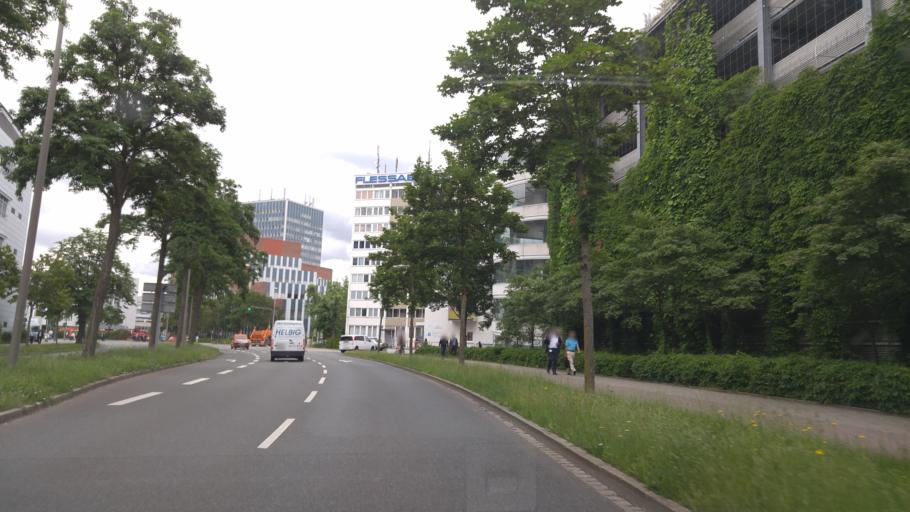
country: DE
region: Bavaria
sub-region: Regierungsbezirk Mittelfranken
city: Erlangen
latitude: 49.5891
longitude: 11.0116
